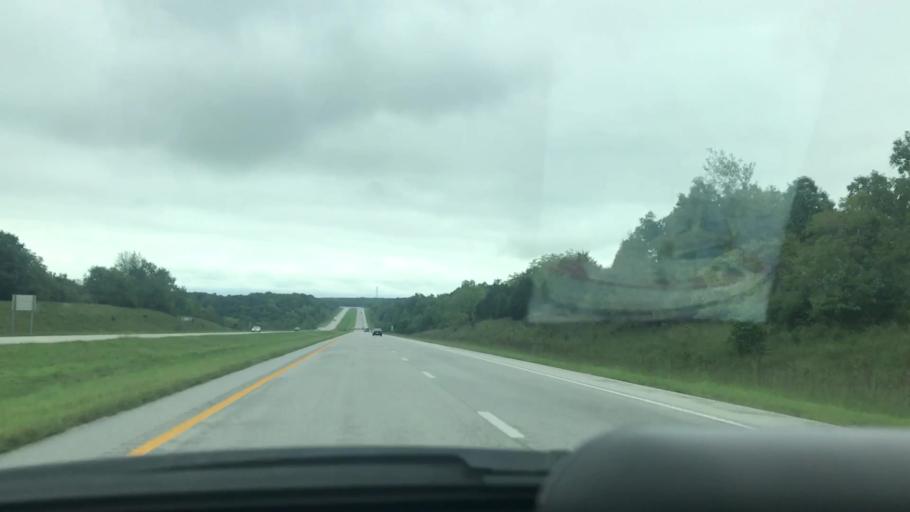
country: US
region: Missouri
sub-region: Greene County
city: Strafford
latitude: 37.3041
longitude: -93.1755
